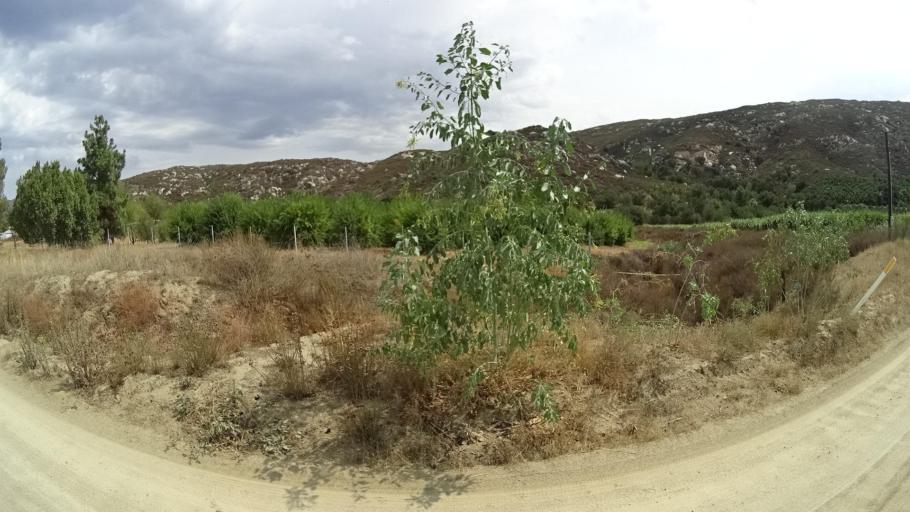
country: US
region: California
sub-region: San Diego County
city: Ramona
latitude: 33.0912
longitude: -116.8316
